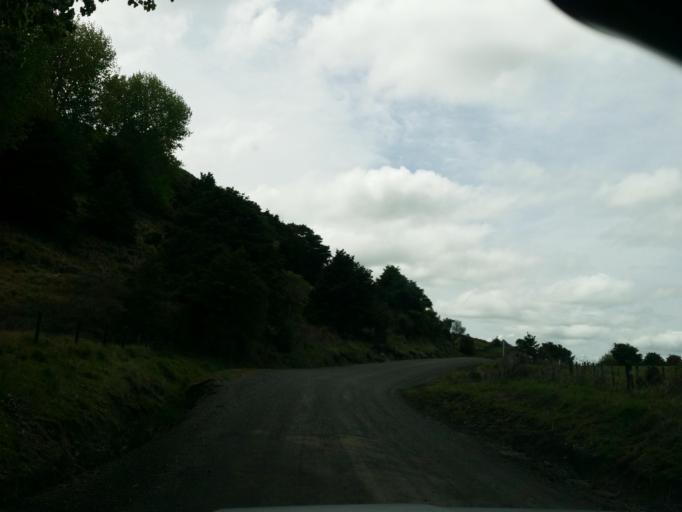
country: NZ
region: Northland
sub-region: Whangarei
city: Maungatapere
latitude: -35.9020
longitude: 174.1195
